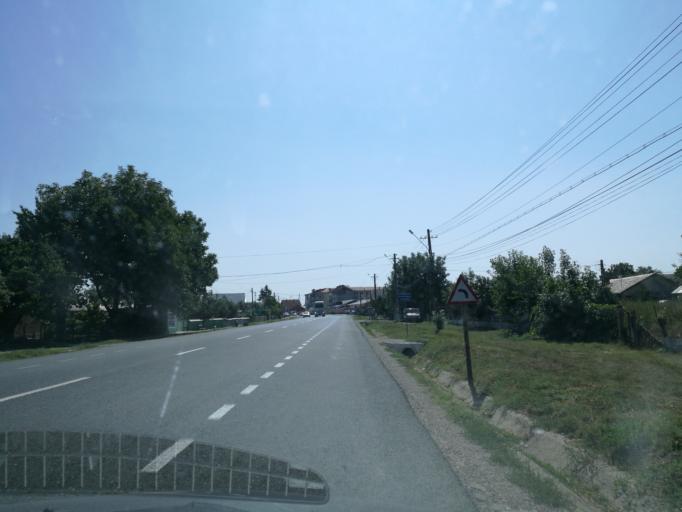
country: RO
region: Bacau
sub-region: Comuna Racaciuni
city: Racaciuni
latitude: 46.3363
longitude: 27.0021
